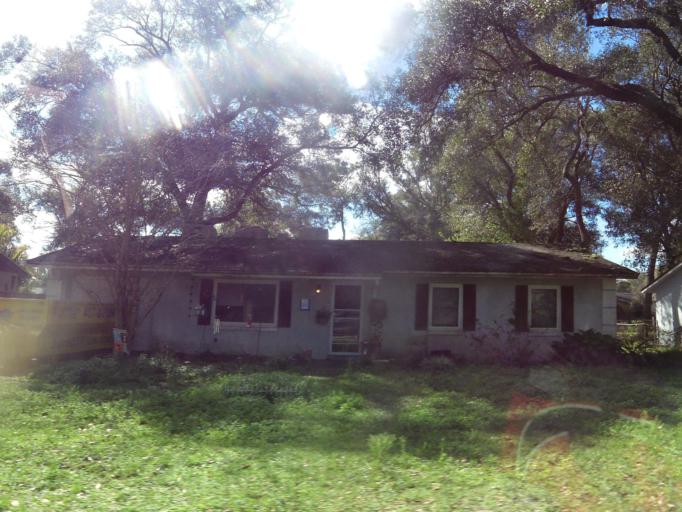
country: US
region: Florida
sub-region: Volusia County
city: Orange City
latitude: 28.9481
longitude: -81.3128
